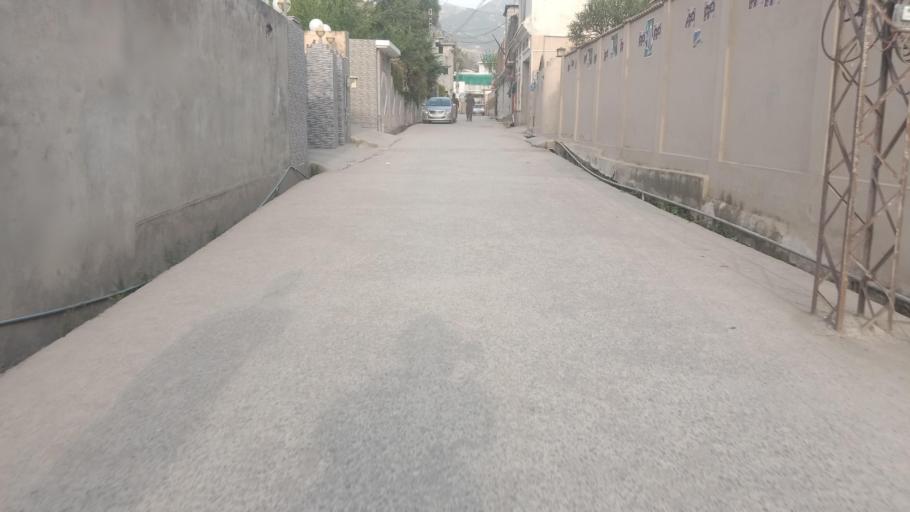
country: PK
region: Khyber Pakhtunkhwa
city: Abbottabad
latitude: 34.1691
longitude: 73.2570
